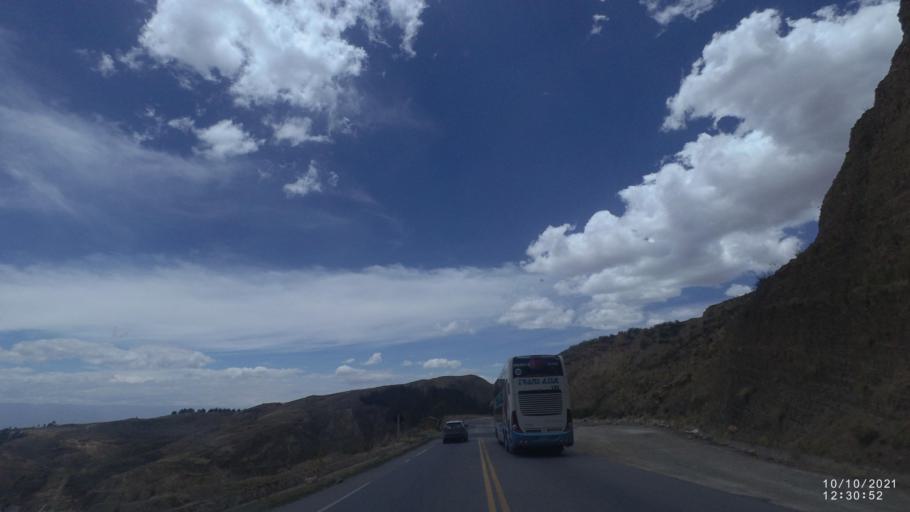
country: BO
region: Cochabamba
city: Irpa Irpa
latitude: -17.6751
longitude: -66.4305
